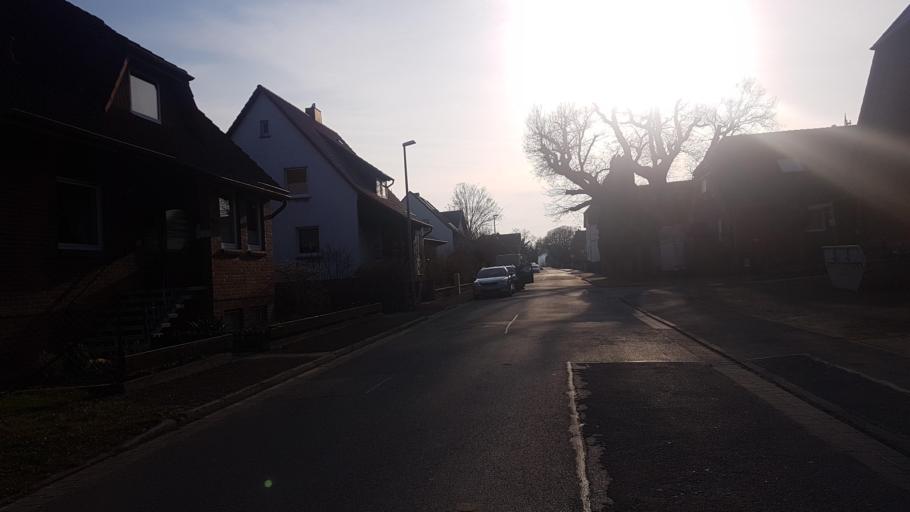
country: DE
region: Lower Saxony
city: Ronnenberg
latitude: 52.2829
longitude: 9.6485
